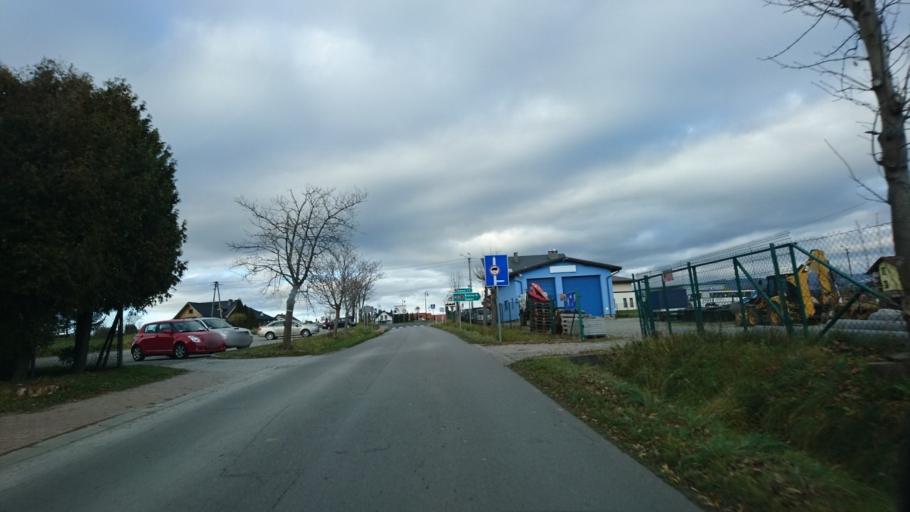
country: PL
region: Silesian Voivodeship
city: Godziszka
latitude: 49.7066
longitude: 19.0903
